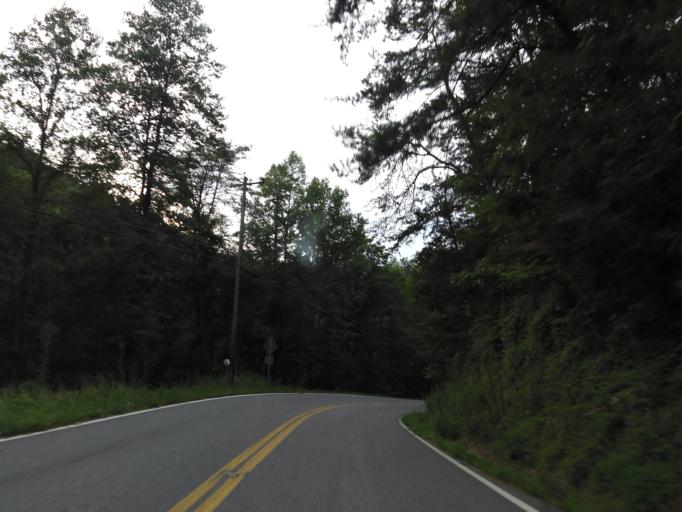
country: US
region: Tennessee
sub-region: Anderson County
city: Rocky Top
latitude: 36.1619
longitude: -84.1931
